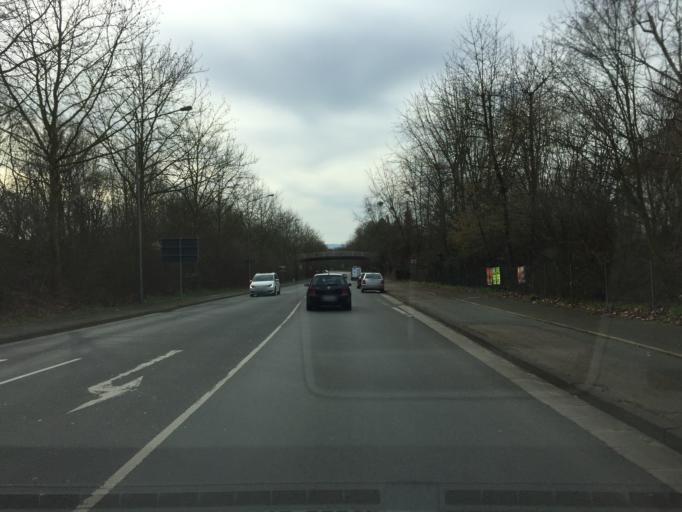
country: DE
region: North Rhine-Westphalia
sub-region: Regierungsbezirk Detmold
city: Bad Salzuflen
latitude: 52.0825
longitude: 8.7565
